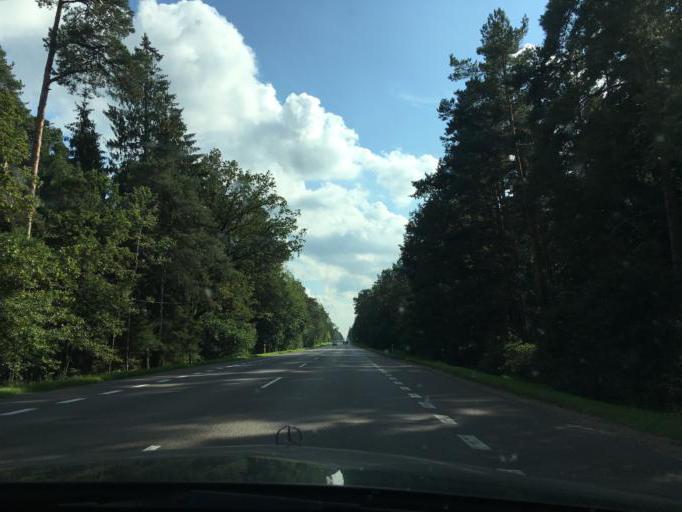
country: PL
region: Podlasie
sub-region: Suwalki
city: Suwalki
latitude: 54.0609
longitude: 22.9351
